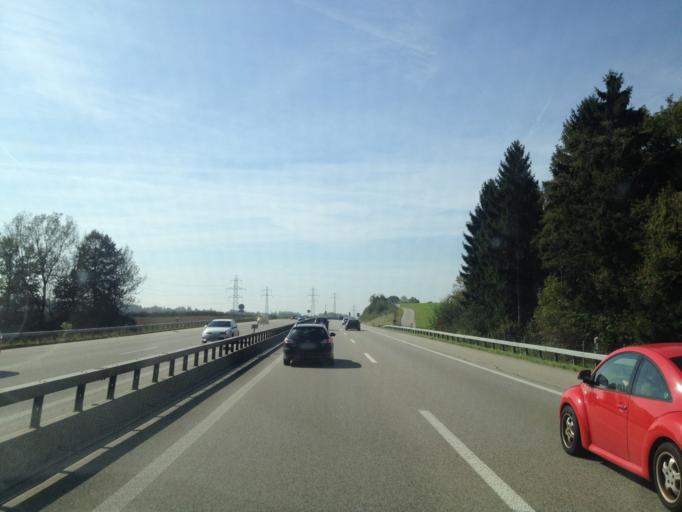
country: CH
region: Bern
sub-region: Oberaargau
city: Oberbipp
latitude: 47.2527
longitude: 7.6733
